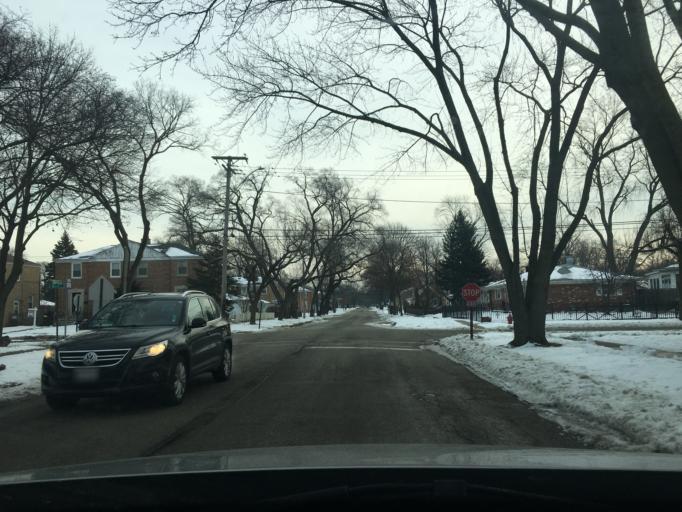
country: US
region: Illinois
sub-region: Cook County
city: Des Plaines
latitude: 42.0206
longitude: -87.8849
